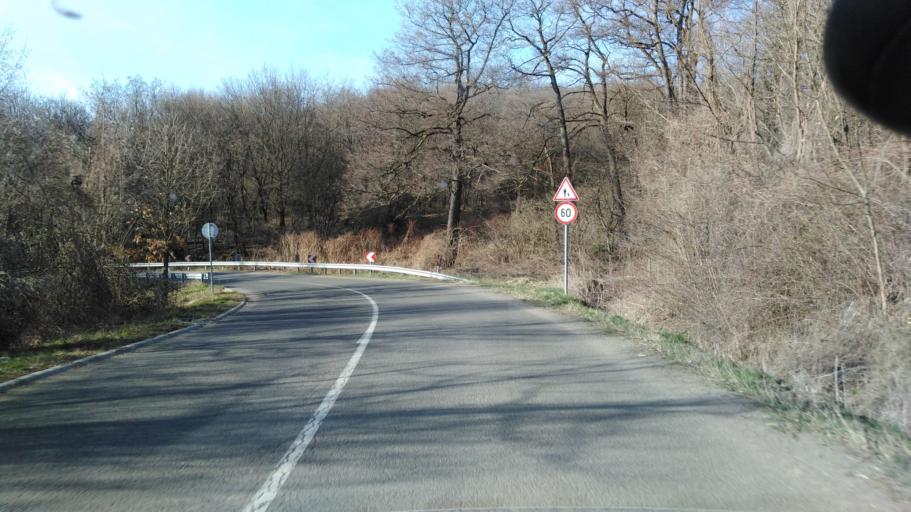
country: HU
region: Nograd
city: Somoskoujfalu
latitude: 48.1607
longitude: 19.8457
